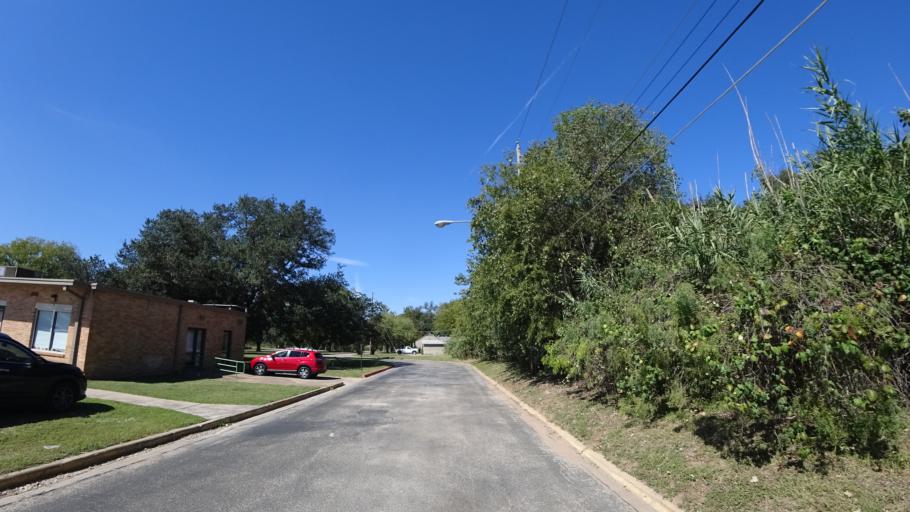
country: US
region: Texas
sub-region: Travis County
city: Hornsby Bend
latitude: 30.2741
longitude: -97.6372
